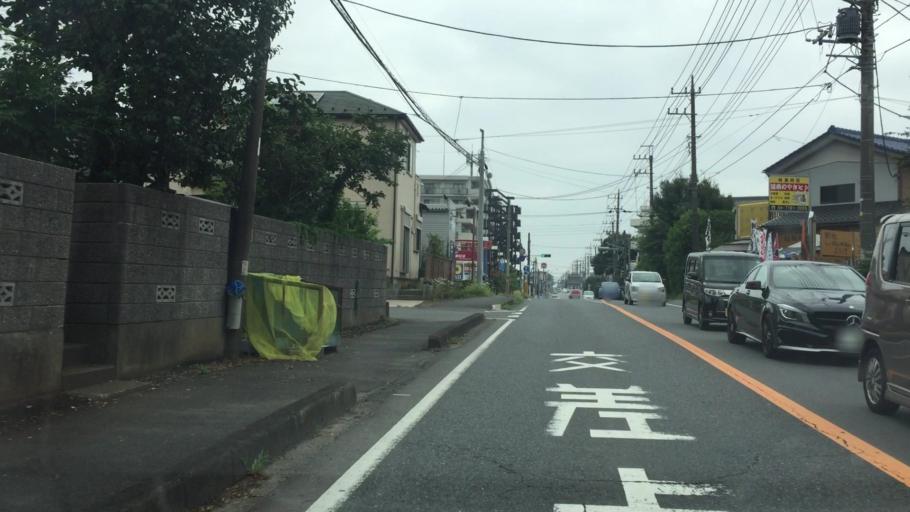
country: JP
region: Chiba
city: Abiko
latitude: 35.8366
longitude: 140.0060
